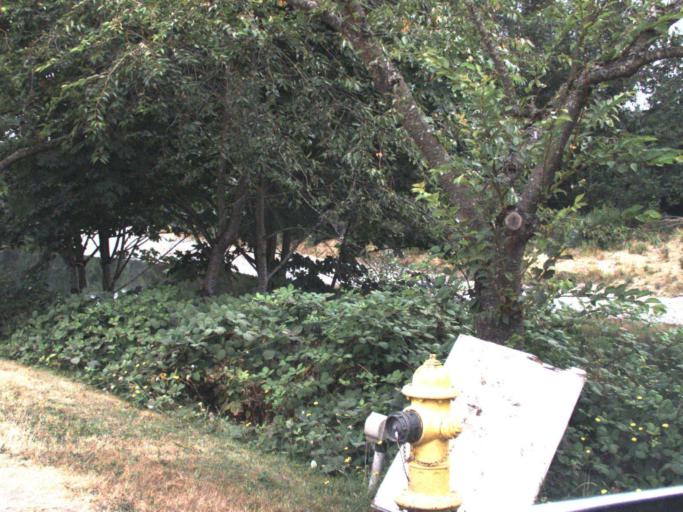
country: US
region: Washington
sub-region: King County
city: Fall City
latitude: 47.5680
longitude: -121.8903
